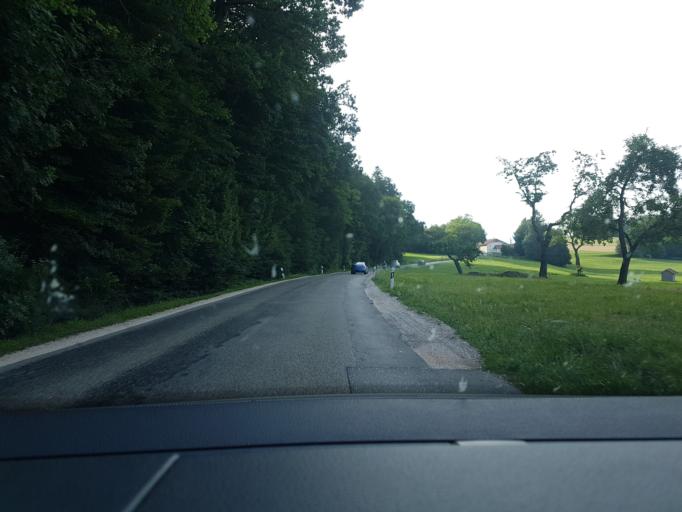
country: DE
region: Bavaria
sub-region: Upper Bavaria
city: Ainring
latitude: 47.8624
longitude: 12.9107
